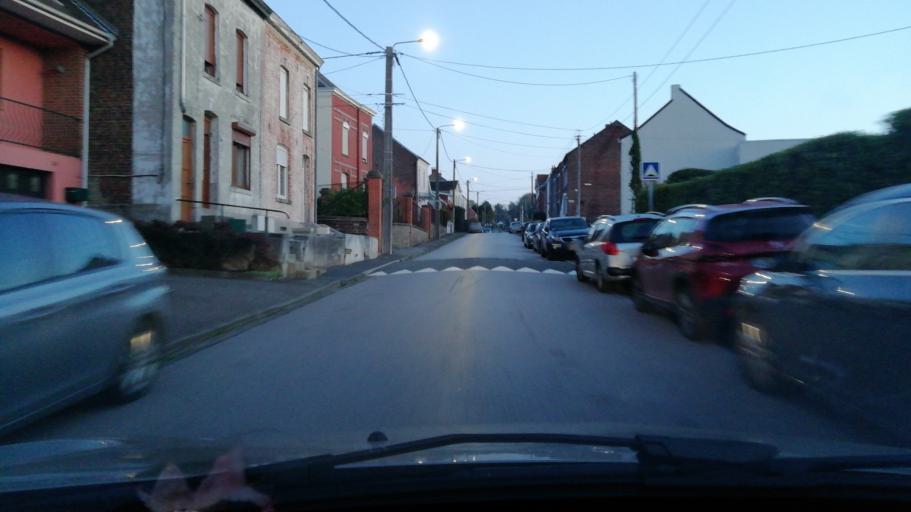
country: FR
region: Nord-Pas-de-Calais
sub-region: Departement du Nord
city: Marpent
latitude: 50.2905
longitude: 4.0825
